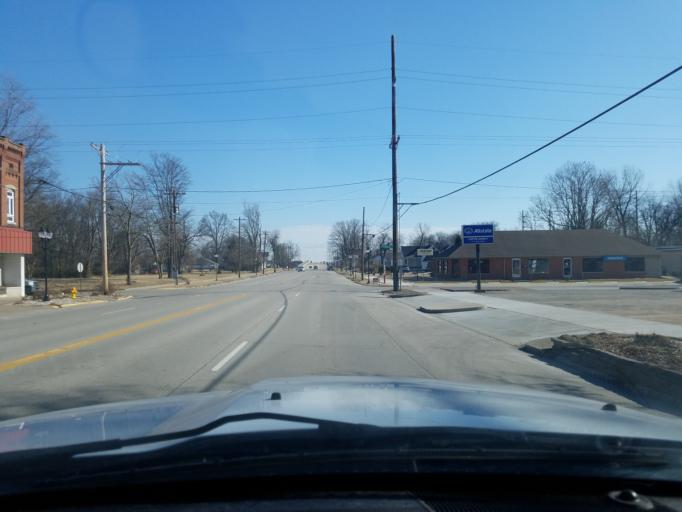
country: US
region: Kentucky
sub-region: Henderson County
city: Henderson
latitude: 37.8373
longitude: -87.5831
